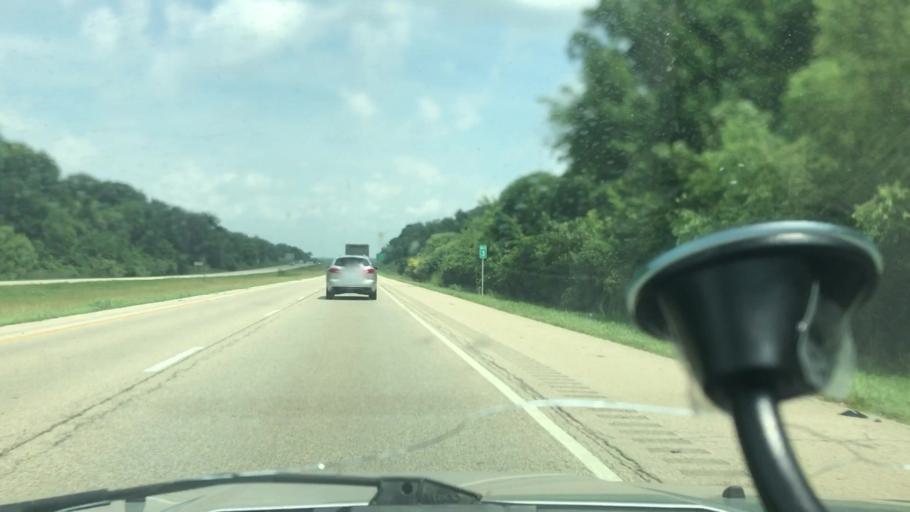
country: US
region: Illinois
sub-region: Peoria County
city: Bellevue
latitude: 40.6993
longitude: -89.6757
